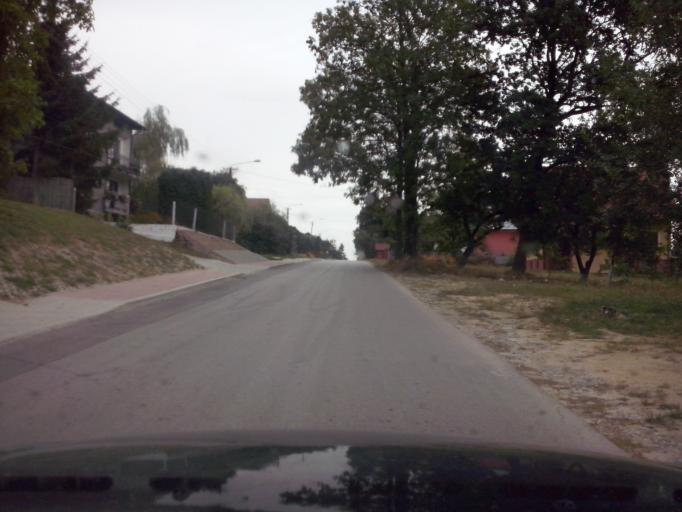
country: PL
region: Swietokrzyskie
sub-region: Powiat kielecki
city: Lagow
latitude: 50.7339
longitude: 21.0807
